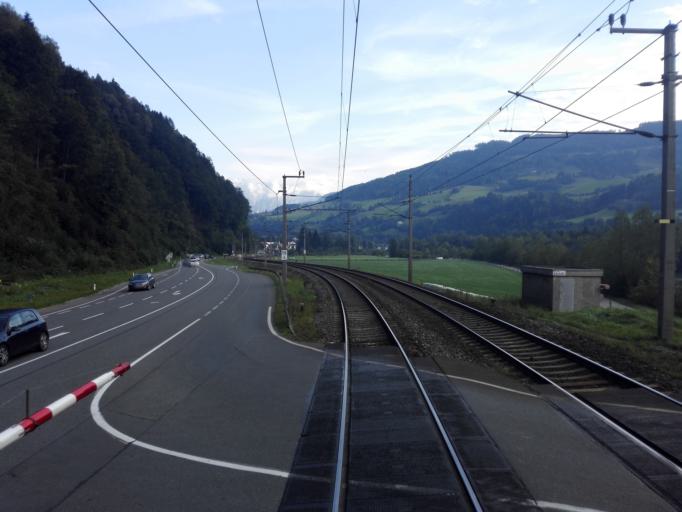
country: AT
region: Salzburg
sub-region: Politischer Bezirk Sankt Johann im Pongau
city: Bischofshofen
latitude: 47.3879
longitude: 13.2135
